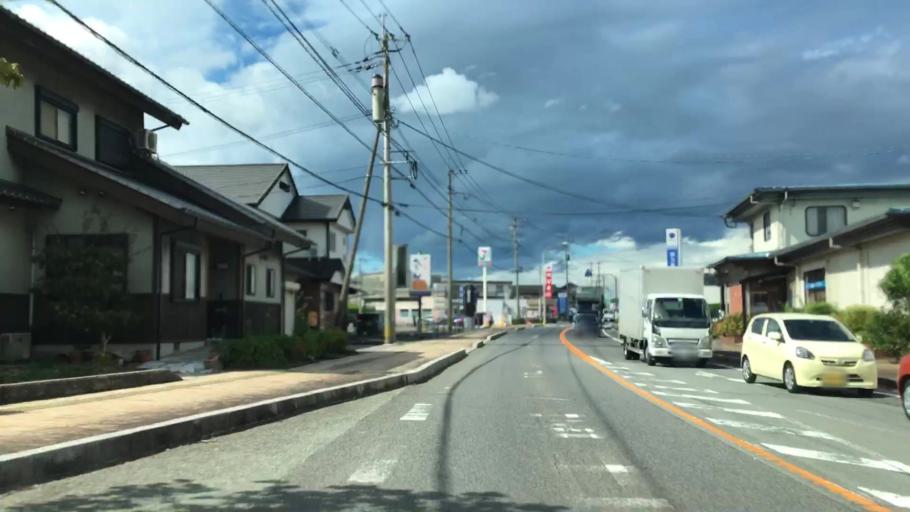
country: JP
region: Saga Prefecture
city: Imaricho-ko
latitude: 33.2109
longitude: 129.8497
